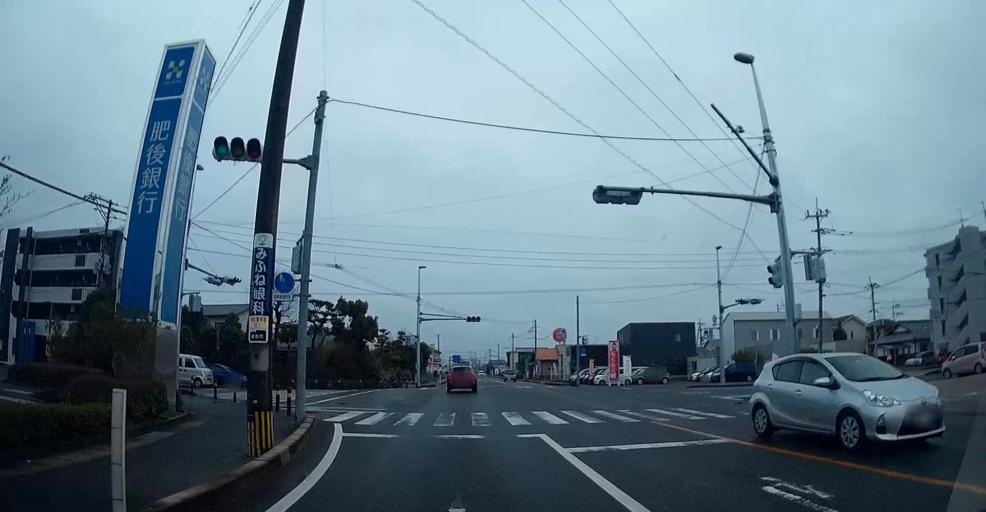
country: JP
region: Kumamoto
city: Kumamoto
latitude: 32.7424
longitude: 130.7405
